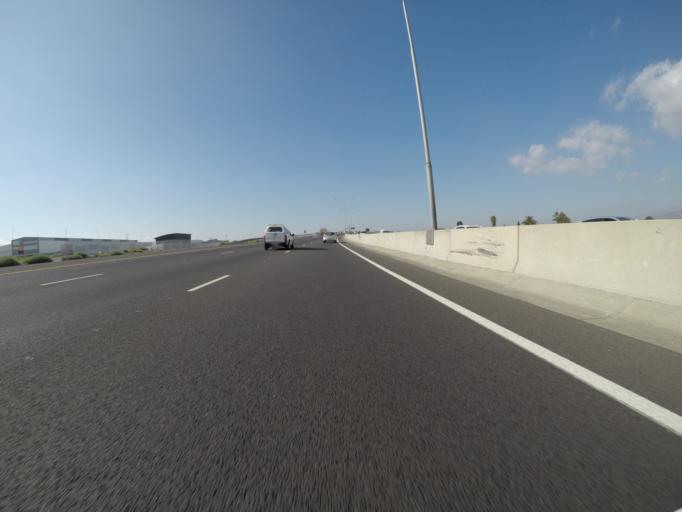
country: ZA
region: Western Cape
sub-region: City of Cape Town
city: Kraaifontein
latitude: -33.9228
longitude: 18.6639
